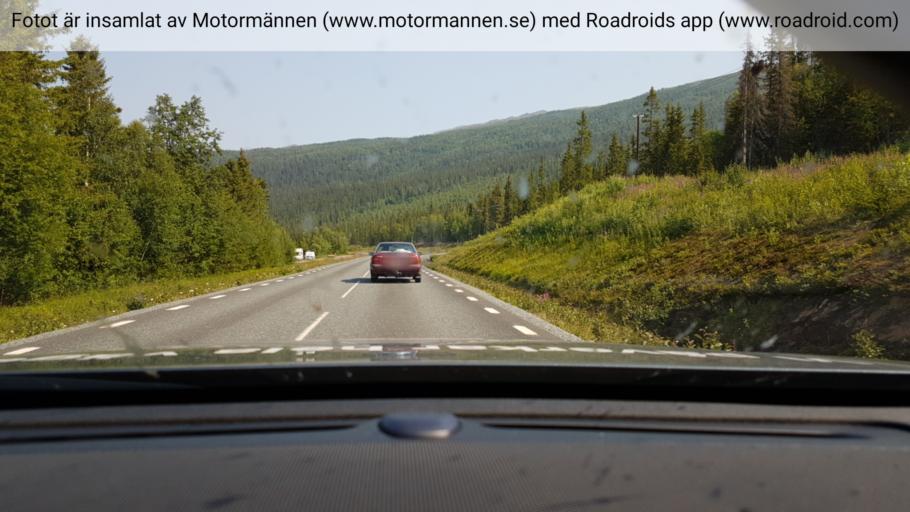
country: SE
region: Vaesterbotten
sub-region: Vilhelmina Kommun
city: Sjoberg
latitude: 65.6235
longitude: 15.5376
